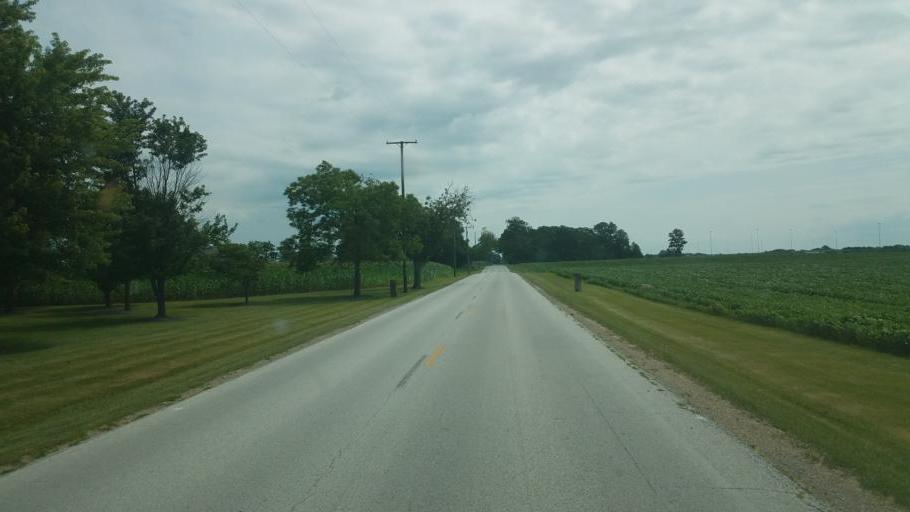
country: US
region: Ohio
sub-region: Wyandot County
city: Upper Sandusky
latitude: 40.8617
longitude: -83.2901
